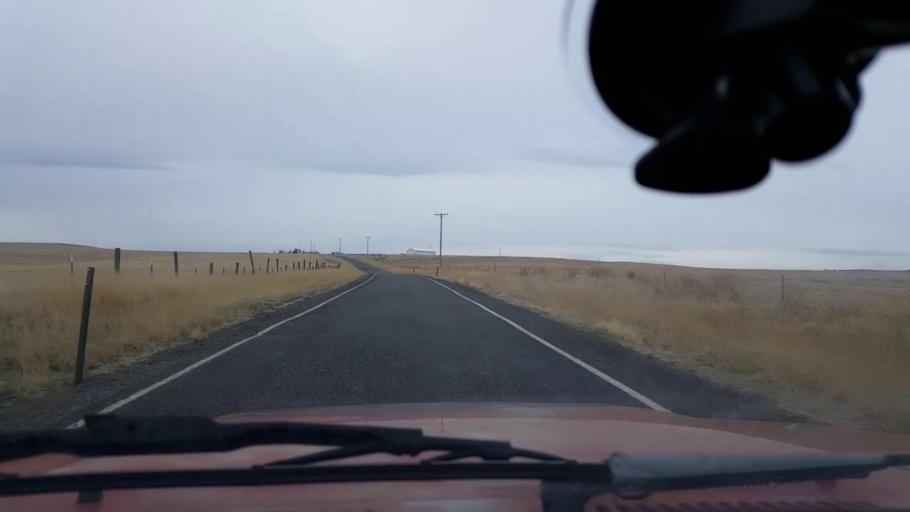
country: US
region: Washington
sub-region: Asotin County
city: Clarkston Heights-Vineland
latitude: 46.3273
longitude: -117.3239
